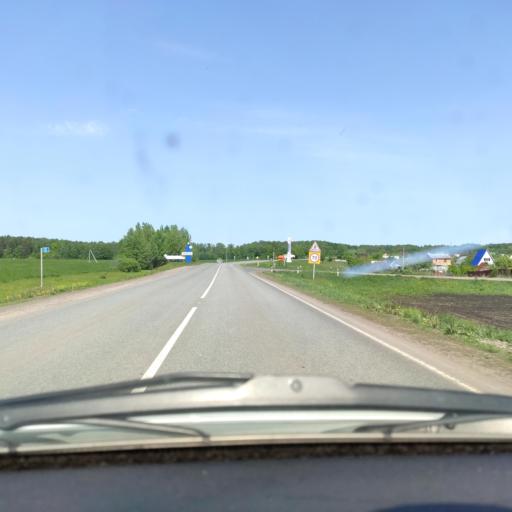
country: RU
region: Bashkortostan
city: Avdon
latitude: 54.5715
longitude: 55.6951
